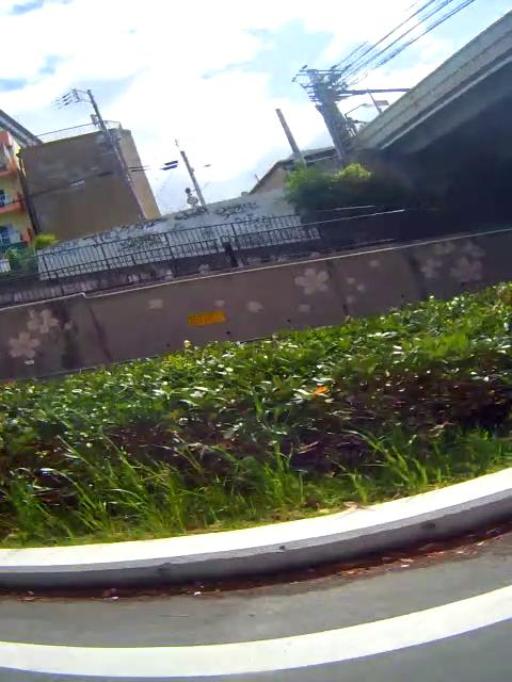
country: JP
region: Osaka
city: Osaka-shi
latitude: 34.7001
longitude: 135.5229
